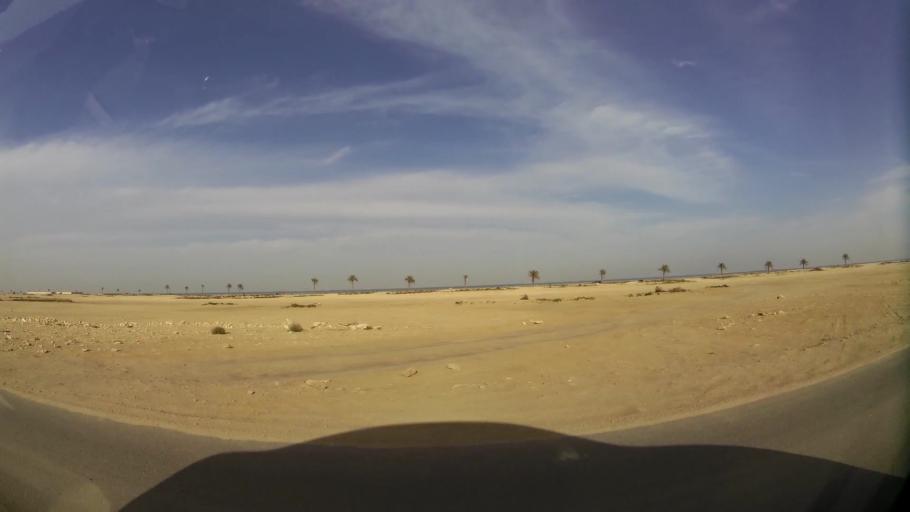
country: QA
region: Al Wakrah
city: Al Wakrah
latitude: 25.1377
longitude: 51.6157
